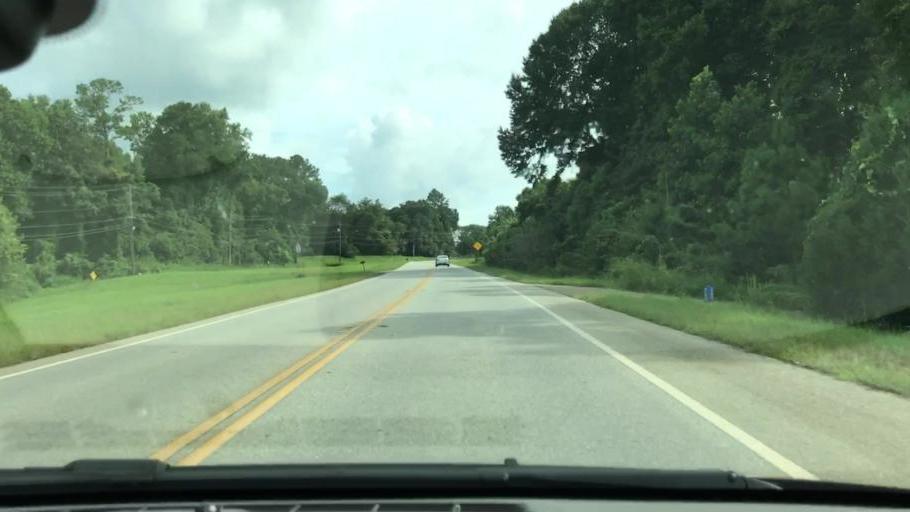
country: US
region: Georgia
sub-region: Clay County
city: Fort Gaines
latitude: 31.6239
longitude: -85.0461
